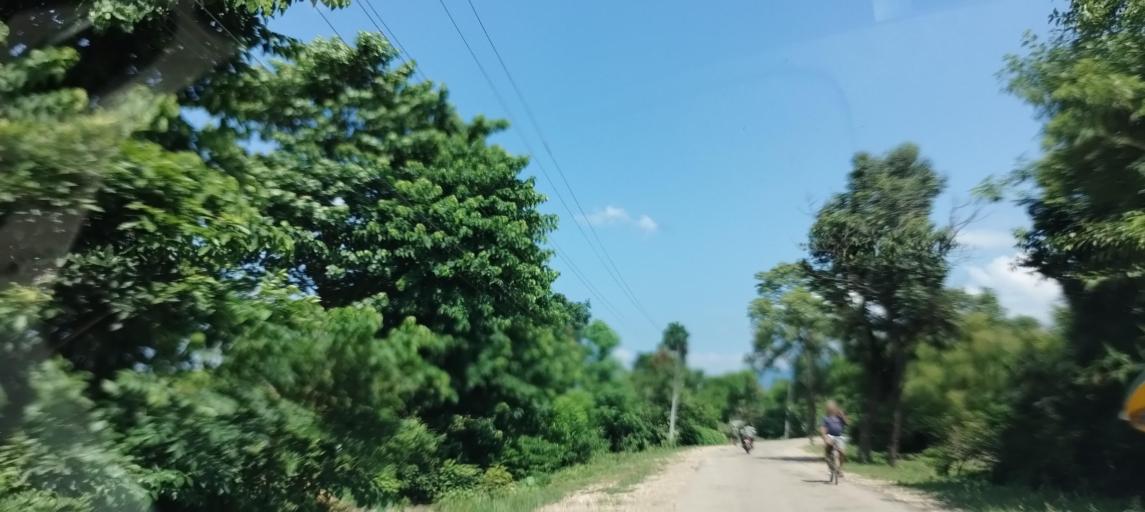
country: NP
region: Far Western
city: Tikapur
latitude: 28.5054
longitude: 81.3027
